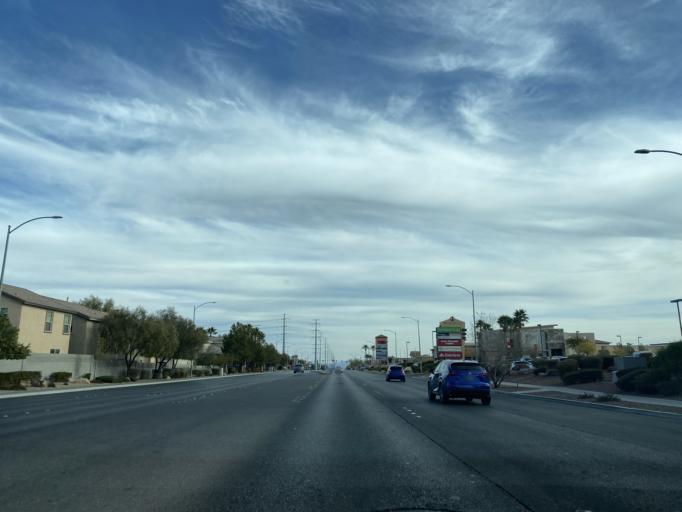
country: US
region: Nevada
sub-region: Clark County
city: Enterprise
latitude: 36.0555
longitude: -115.2837
